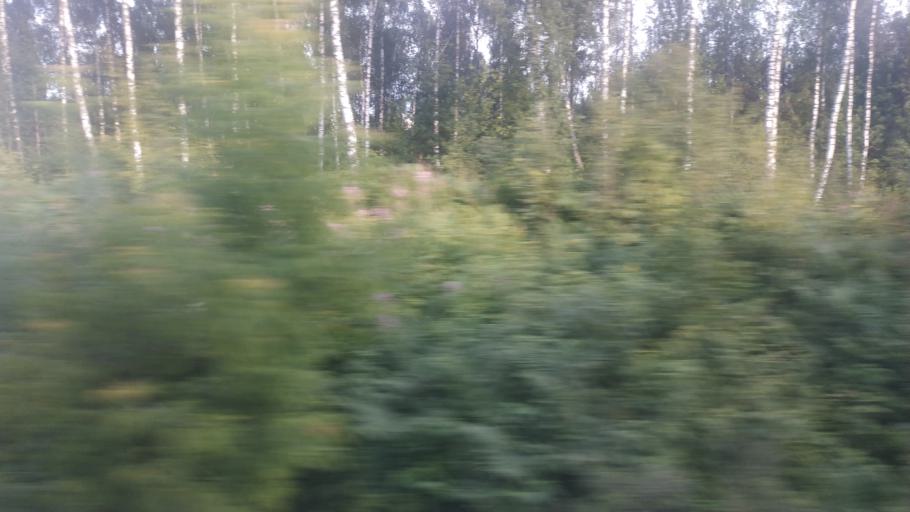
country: RU
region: Moskovskaya
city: Kerva
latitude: 55.5513
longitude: 39.6925
